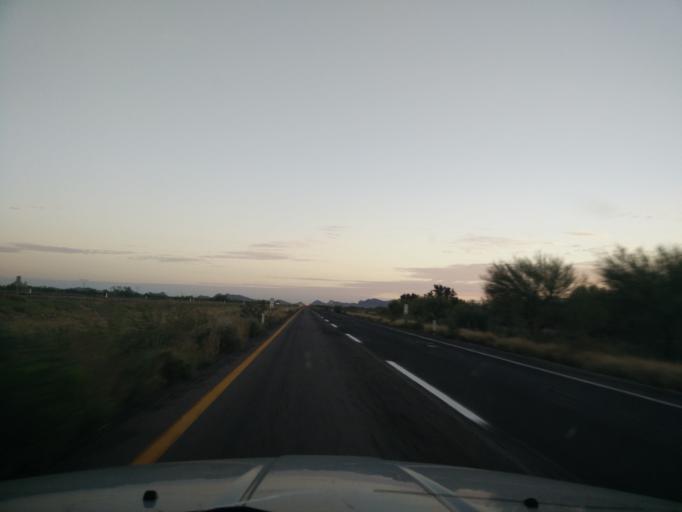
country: MX
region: Sonora
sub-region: Empalme
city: Empalme
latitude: 28.3435
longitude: -111.0424
